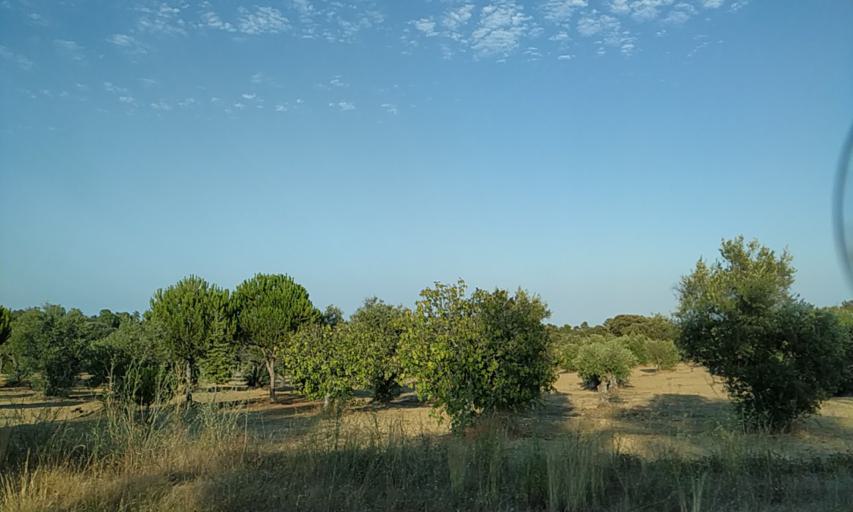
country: PT
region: Santarem
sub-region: Alcanena
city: Alcanena
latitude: 39.4396
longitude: -8.6253
